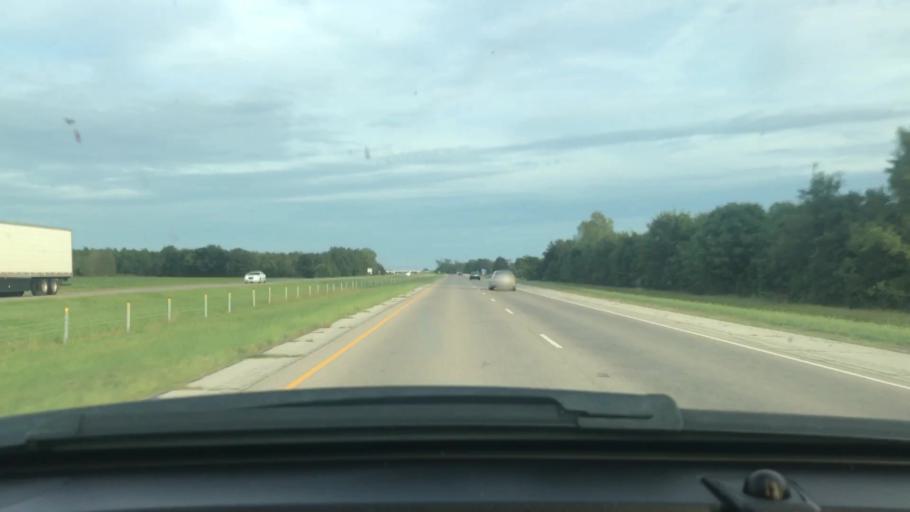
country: US
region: Arkansas
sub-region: Craighead County
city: Bay
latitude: 35.7857
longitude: -90.6024
